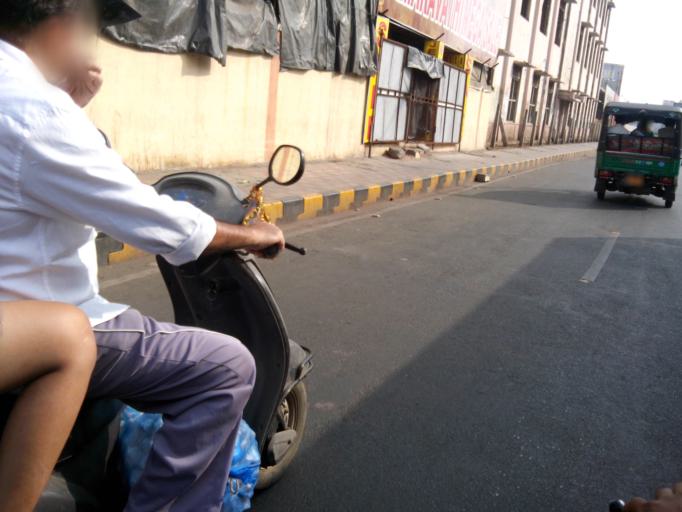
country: IN
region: Andhra Pradesh
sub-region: Krishna
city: Vijayawada
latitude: 16.5114
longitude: 80.6182
